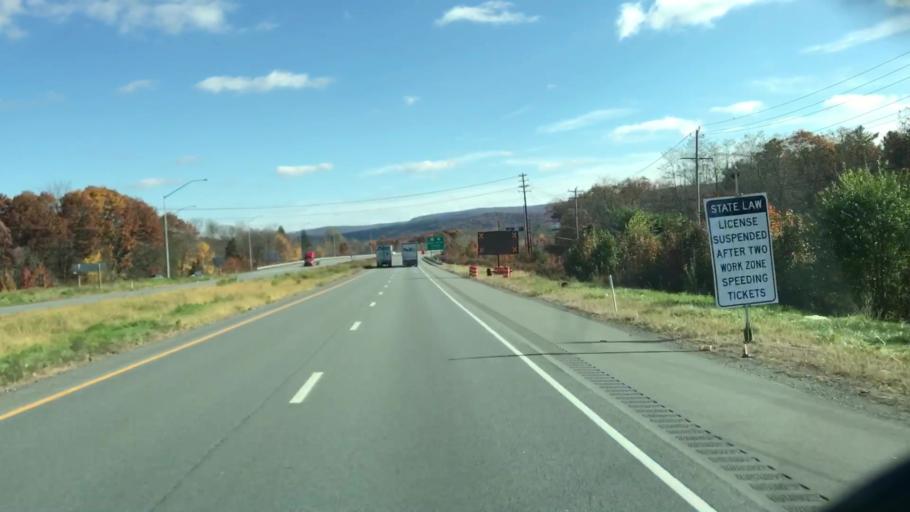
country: US
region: Pennsylvania
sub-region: Pike County
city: Matamoras
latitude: 41.3585
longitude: -74.7079
